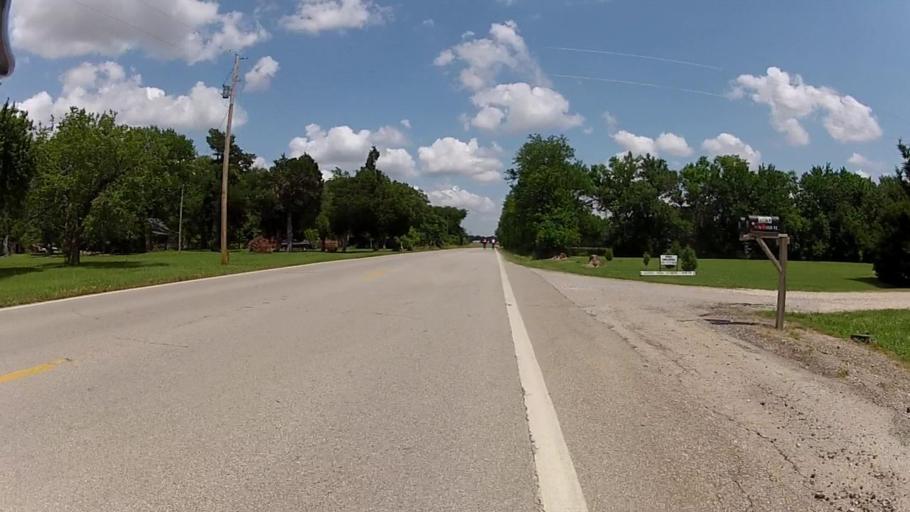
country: US
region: Kansas
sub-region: Labette County
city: Altamont
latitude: 37.1930
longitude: -95.3266
